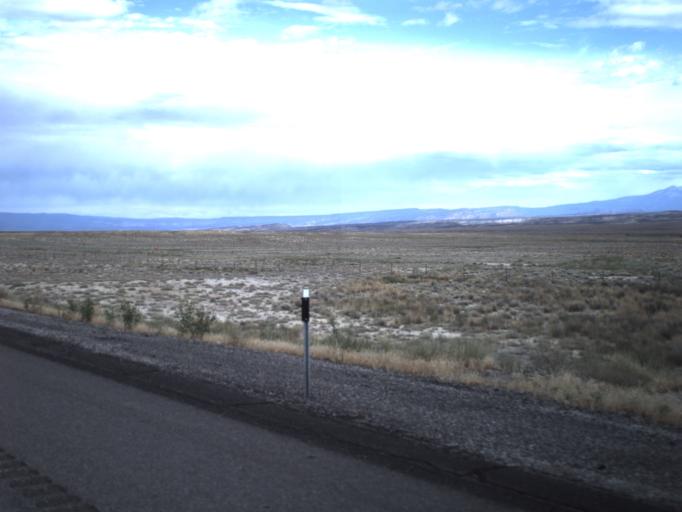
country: US
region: Utah
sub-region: Grand County
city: Moab
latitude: 38.9417
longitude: -109.5450
